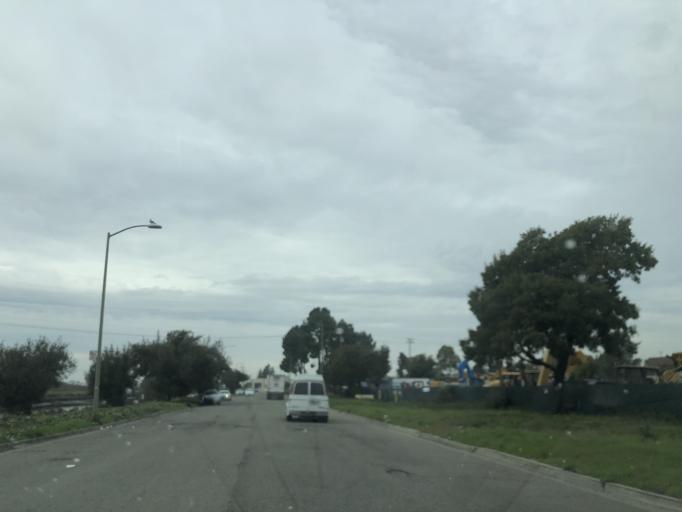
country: US
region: California
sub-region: Alameda County
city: San Leandro
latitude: 37.7334
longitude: -122.1994
